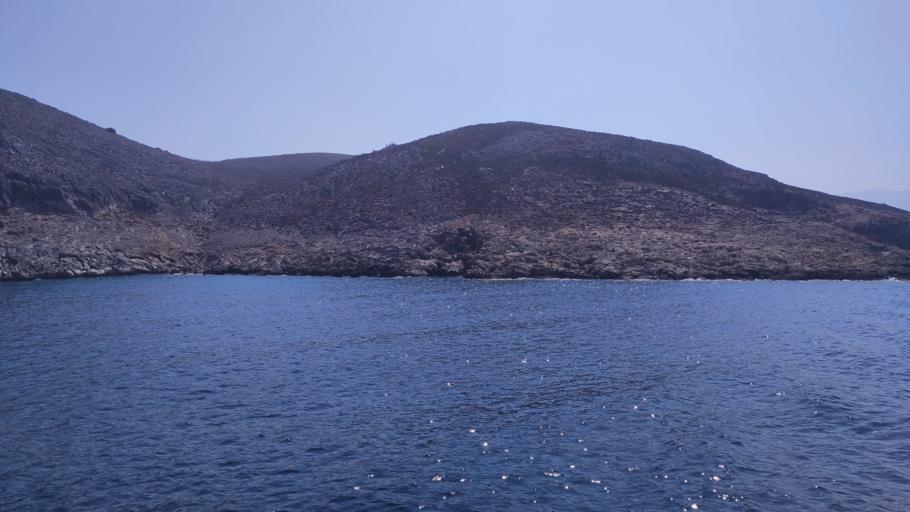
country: GR
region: South Aegean
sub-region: Nomos Dodekanisou
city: Pylion
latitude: 36.9259
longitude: 27.1307
